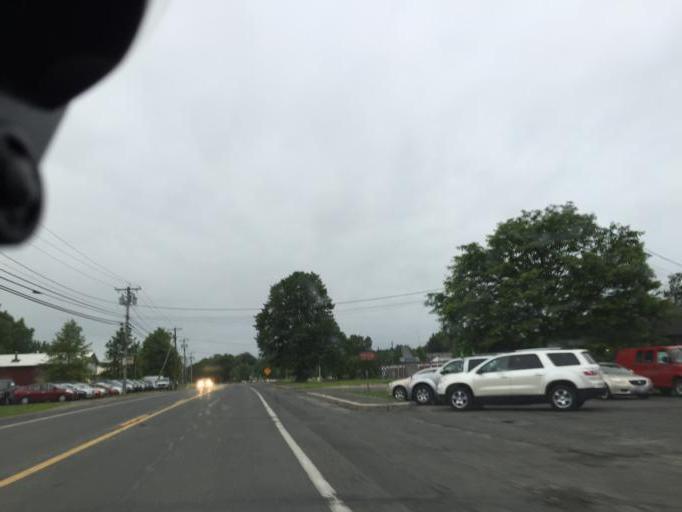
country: US
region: Massachusetts
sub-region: Berkshire County
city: Great Barrington
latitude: 42.1592
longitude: -73.3653
